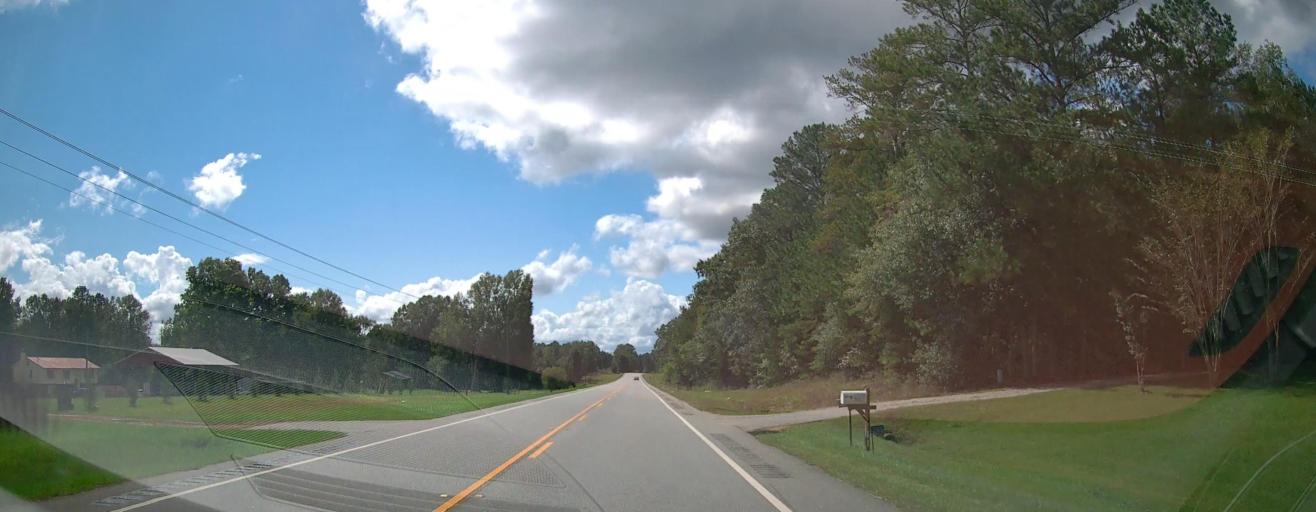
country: US
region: Georgia
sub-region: Baldwin County
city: Milledgeville
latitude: 33.0756
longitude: -83.3136
